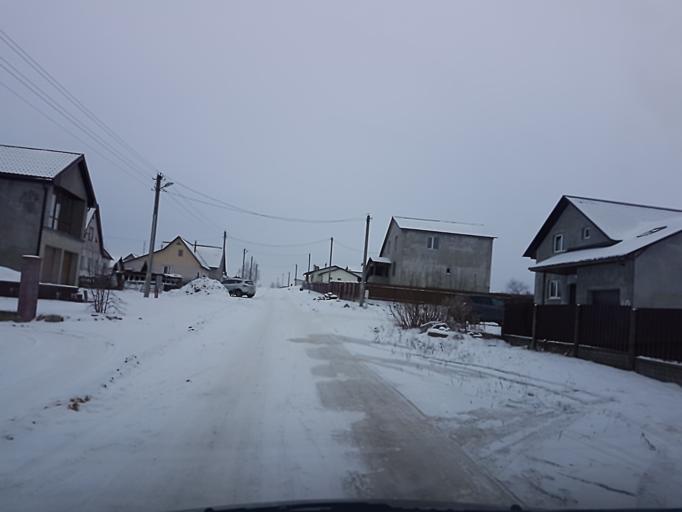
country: BY
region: Minsk
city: Rakaw
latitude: 53.9628
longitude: 27.0370
